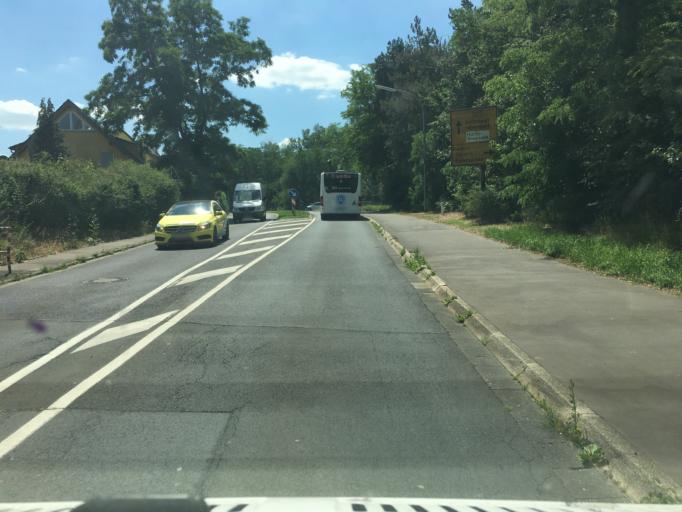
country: DE
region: North Rhine-Westphalia
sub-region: Regierungsbezirk Koln
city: Frechen
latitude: 50.8675
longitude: 6.8150
